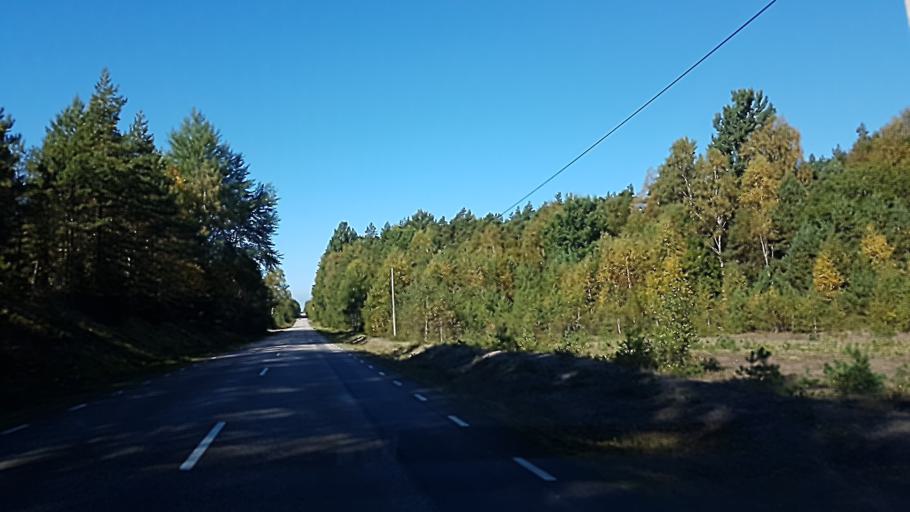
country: SE
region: Kronoberg
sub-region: Ljungby Kommun
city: Ljungby
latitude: 56.8258
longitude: 14.0492
